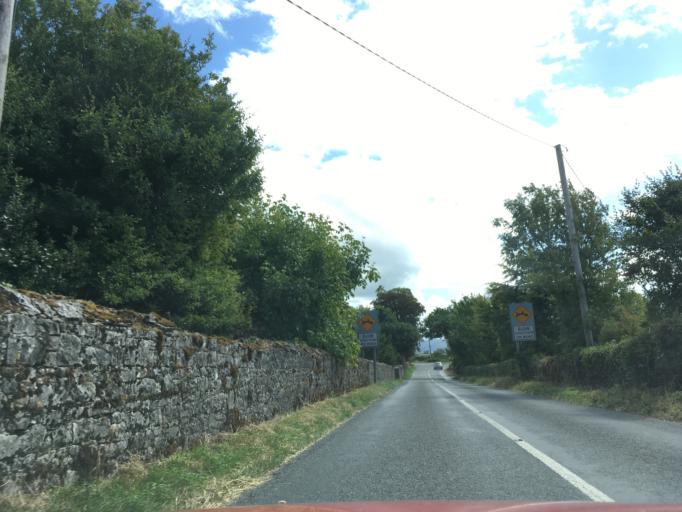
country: IE
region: Munster
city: Cahir
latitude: 52.3501
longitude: -7.9358
